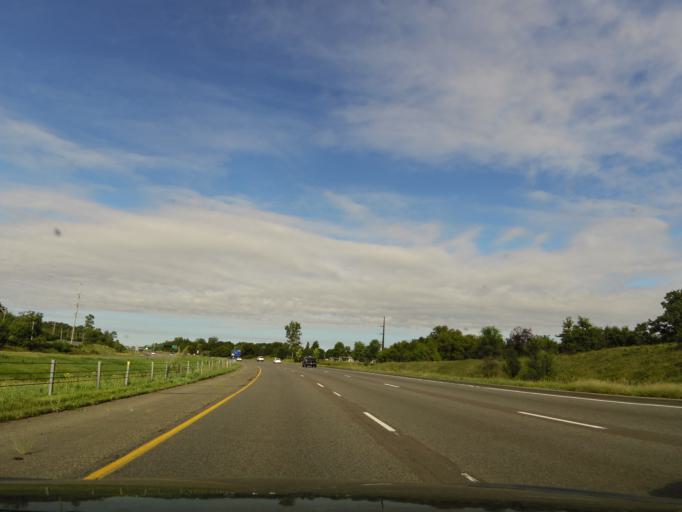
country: US
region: Minnesota
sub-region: Dakota County
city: Mendota Heights
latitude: 44.8620
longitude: -93.1086
